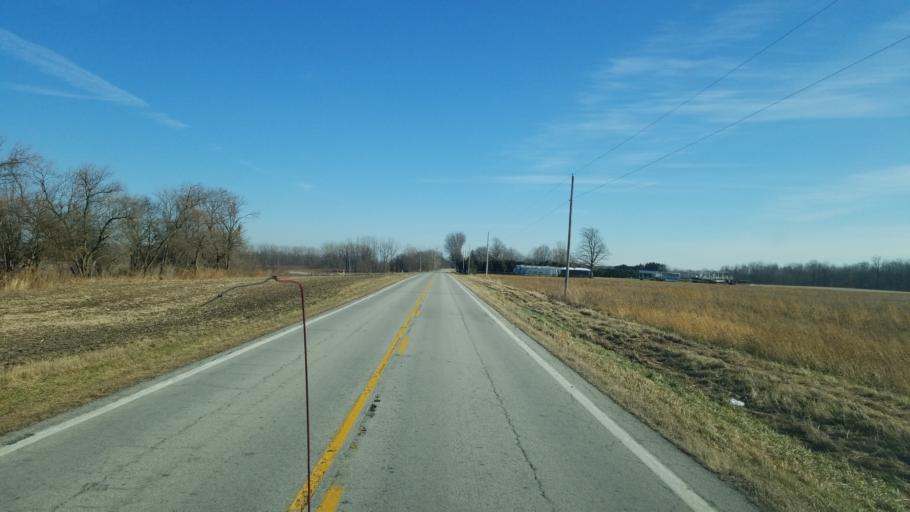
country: US
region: Ohio
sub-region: Henry County
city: Liberty Center
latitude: 41.4152
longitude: -83.9534
